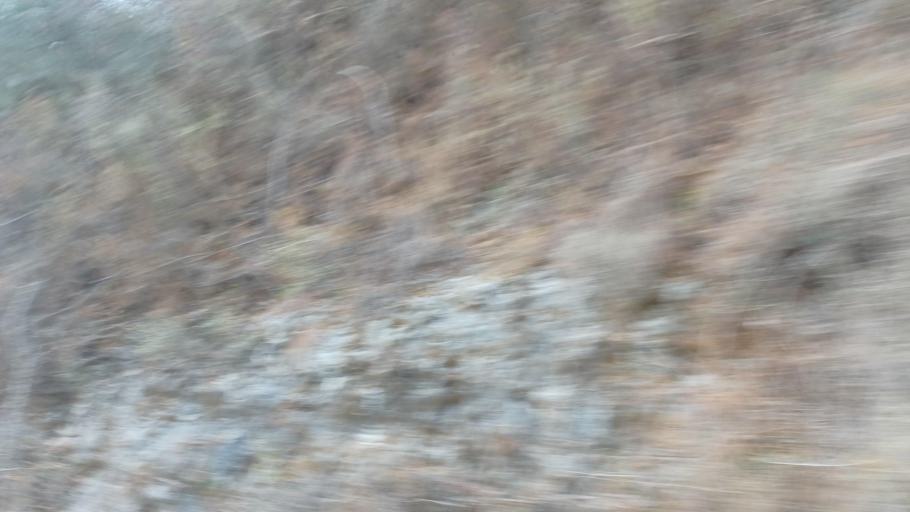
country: CY
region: Pafos
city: Tala
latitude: 34.9125
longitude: 32.4975
